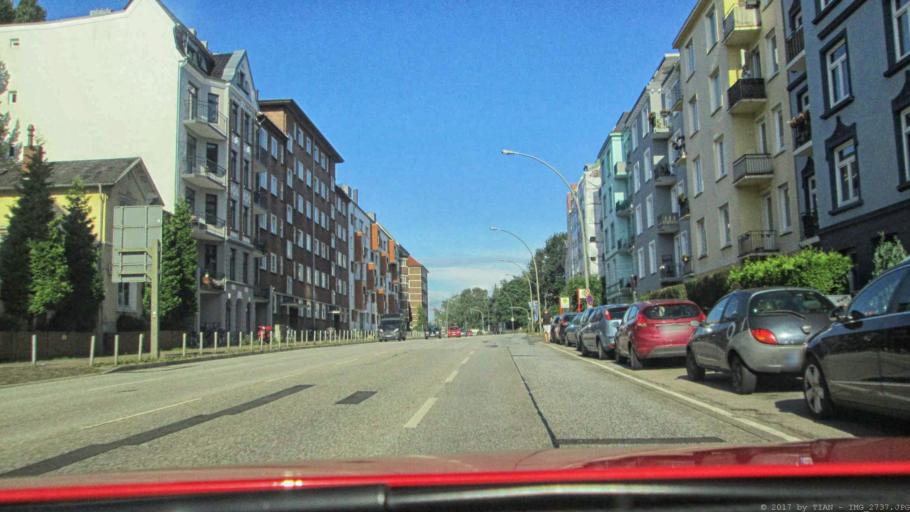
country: DE
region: Hamburg
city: Hamburg-Nord
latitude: 53.5970
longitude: 9.9800
